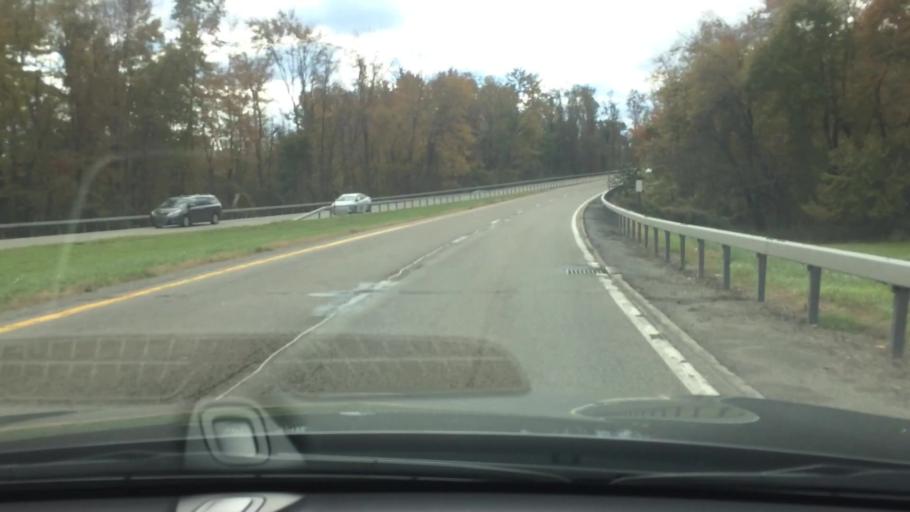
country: US
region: New York
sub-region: Dutchess County
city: Hillside Lake
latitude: 41.5720
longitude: -73.7800
